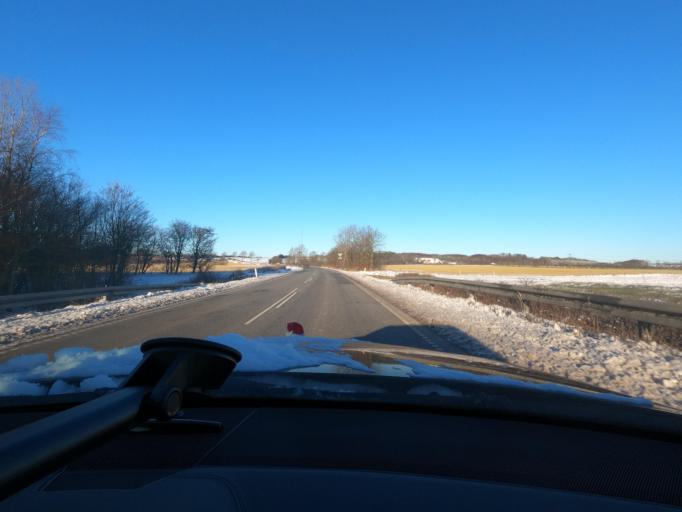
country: DK
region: South Denmark
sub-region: Aabenraa Kommune
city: Rodekro
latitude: 55.0792
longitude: 9.2205
